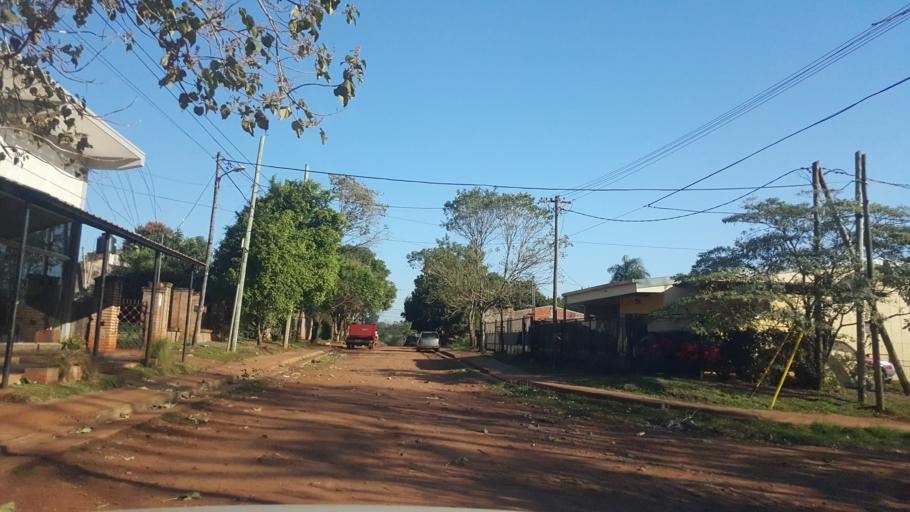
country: AR
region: Misiones
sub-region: Departamento de Capital
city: Posadas
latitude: -27.4066
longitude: -55.9378
